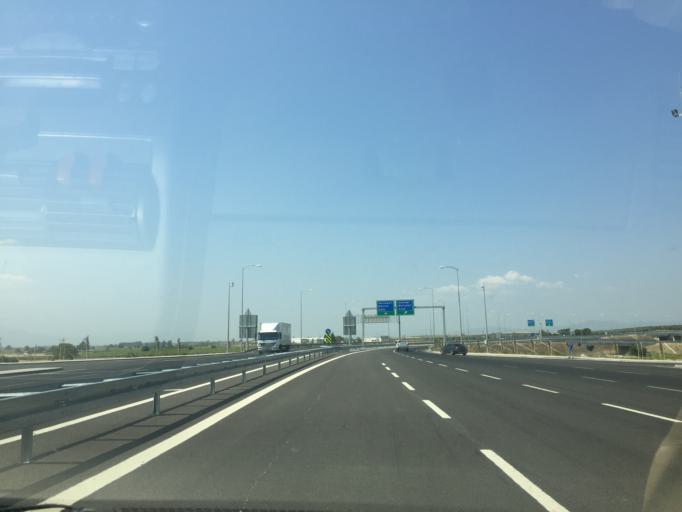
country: TR
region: Manisa
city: Halitpasa
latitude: 38.7640
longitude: 27.6538
